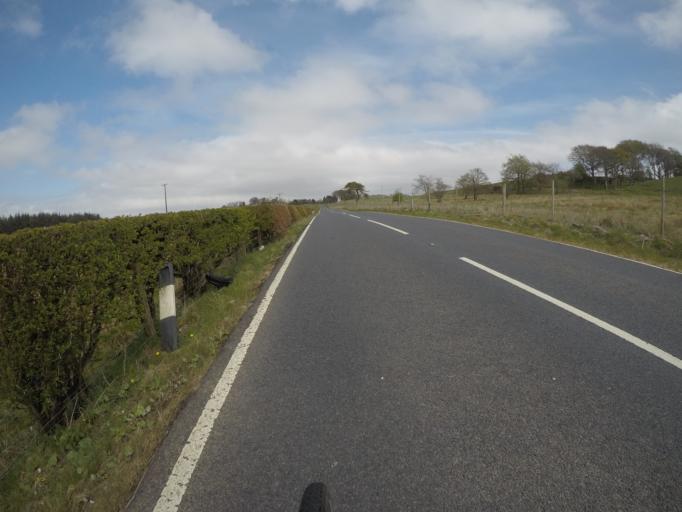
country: GB
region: Scotland
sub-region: East Renfrewshire
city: Neilston
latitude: 55.7229
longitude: -4.4298
